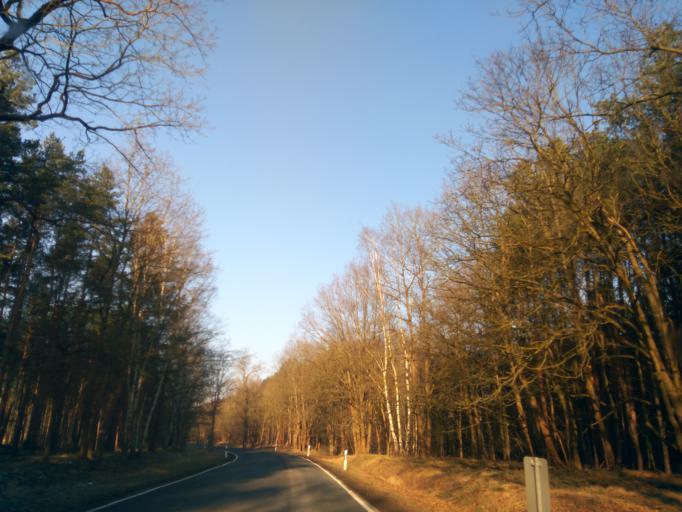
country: DE
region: Brandenburg
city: Falkensee
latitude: 52.6202
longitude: 13.0970
